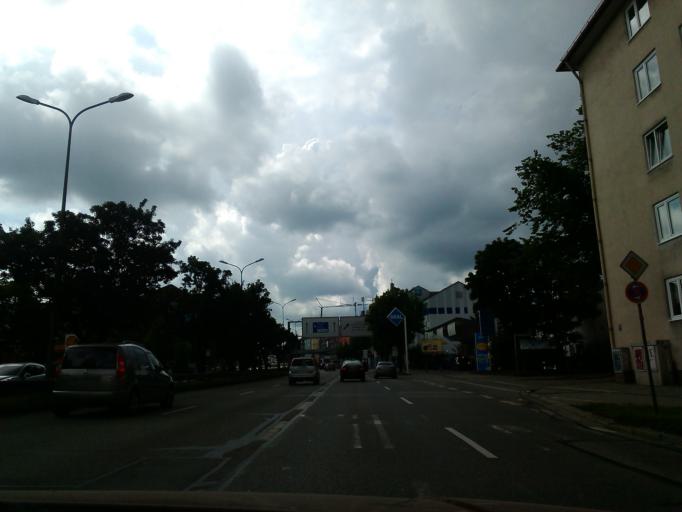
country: DE
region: Bavaria
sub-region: Upper Bavaria
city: Munich
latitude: 48.1083
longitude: 11.5793
